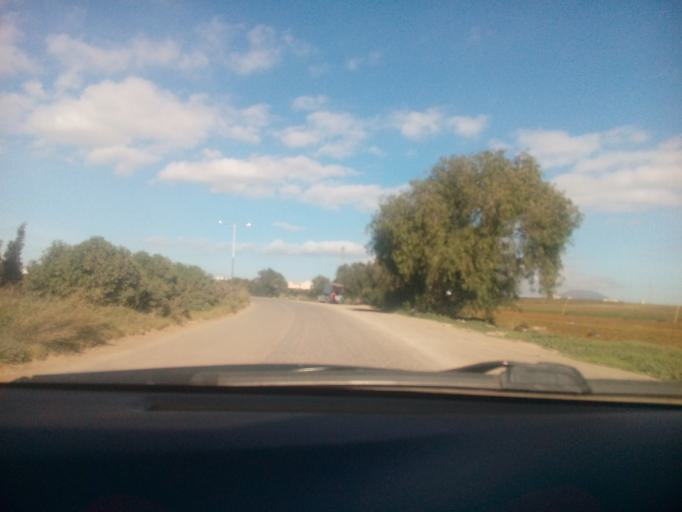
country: DZ
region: Oran
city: Sidi ech Chahmi
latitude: 35.6752
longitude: -0.5656
